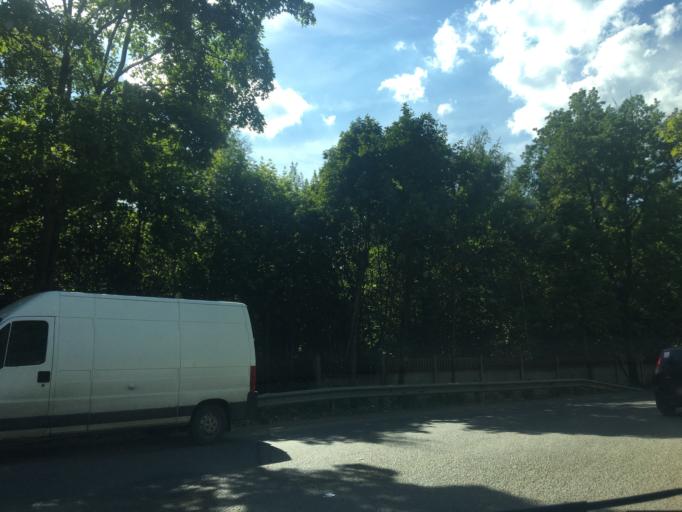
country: RU
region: Moscow
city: Zagor'ye
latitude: 55.5278
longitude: 37.6630
